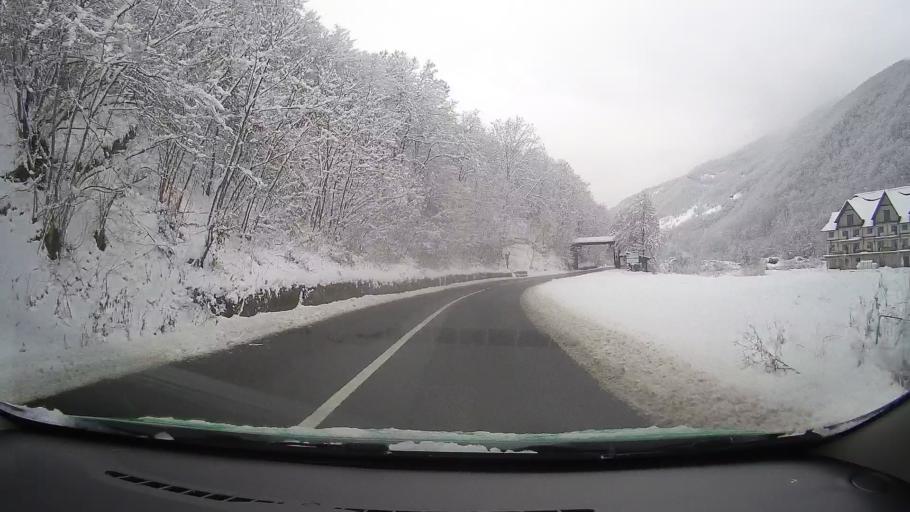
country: RO
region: Alba
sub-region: Comuna Sugag
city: Sugag
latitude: 45.8065
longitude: 23.6247
